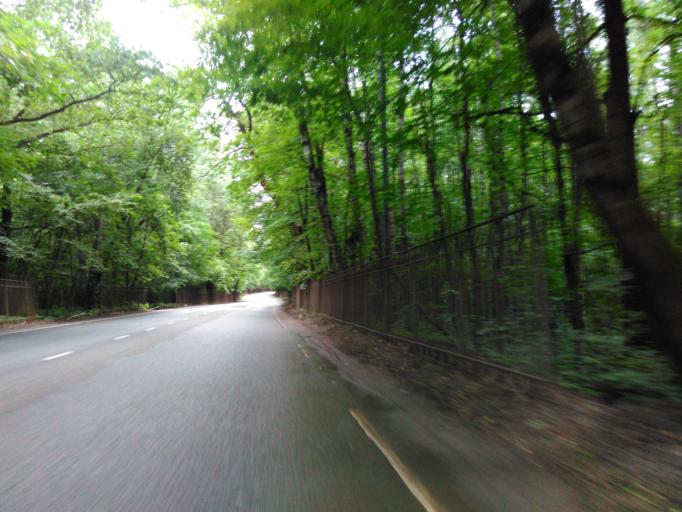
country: RU
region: Moscow
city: Rostokino
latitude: 55.8300
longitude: 37.6916
